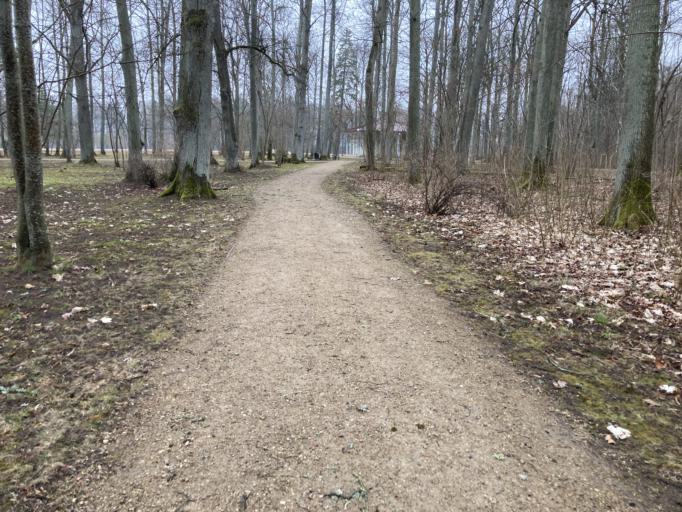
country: LT
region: Siauliu apskritis
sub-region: Joniskis
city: Joniskis
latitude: 56.4254
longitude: 23.7011
